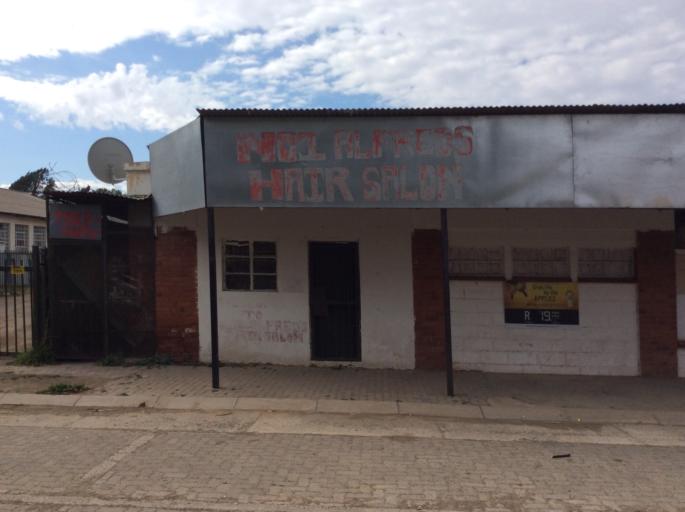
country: LS
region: Mafeteng
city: Mafeteng
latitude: -29.7269
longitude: 27.0389
